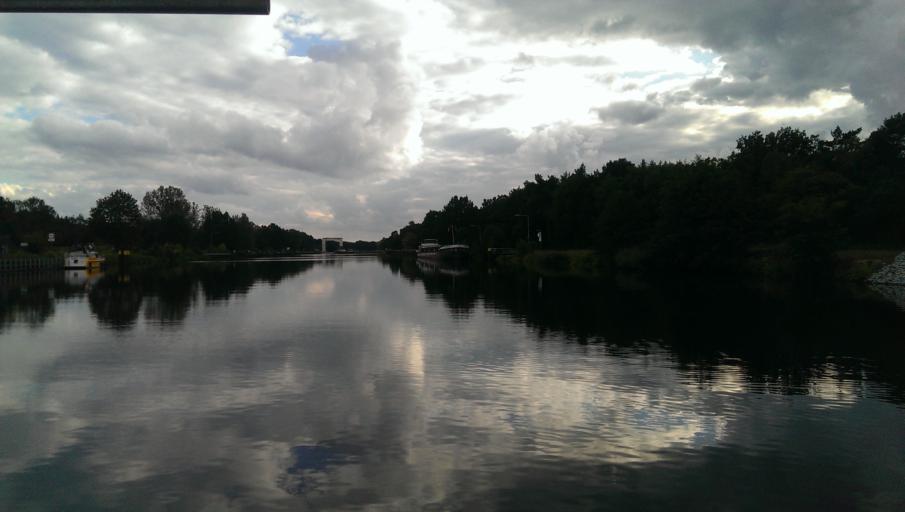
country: DE
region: Brandenburg
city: Oranienburg
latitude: 52.7751
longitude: 13.2801
